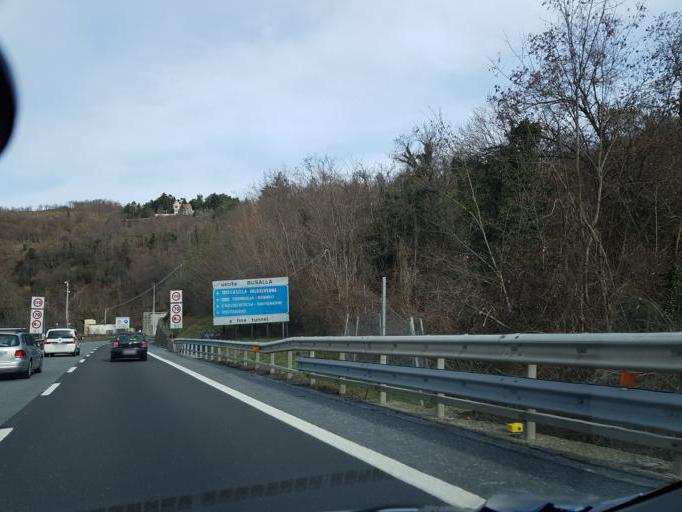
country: IT
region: Liguria
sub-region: Provincia di Genova
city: Busalla
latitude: 44.5490
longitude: 8.9449
